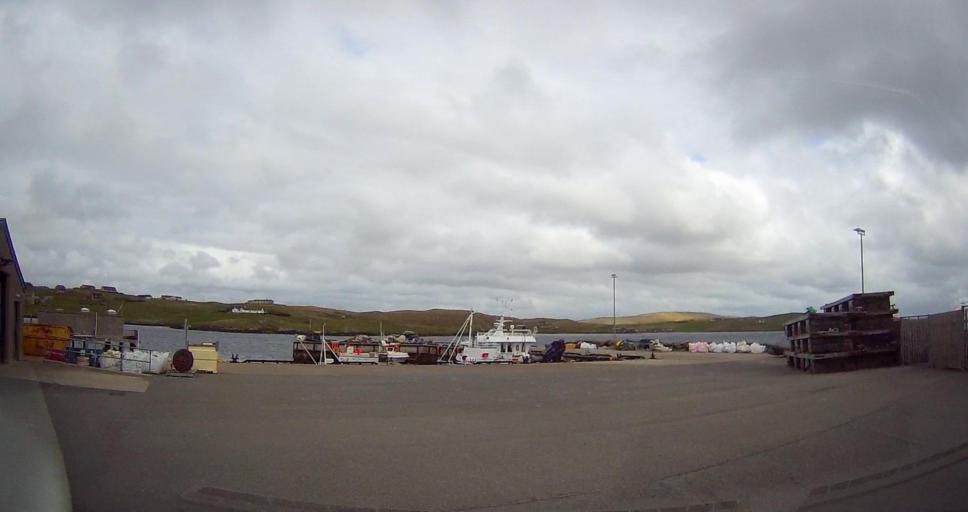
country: GB
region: Scotland
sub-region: Shetland Islands
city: Sandwick
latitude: 60.2239
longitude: -1.5698
